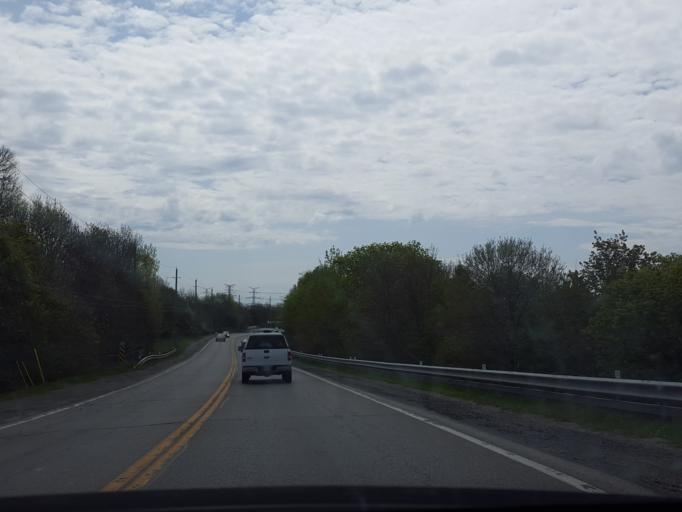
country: CA
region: Ontario
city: Oshawa
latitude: 43.9022
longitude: -78.6967
